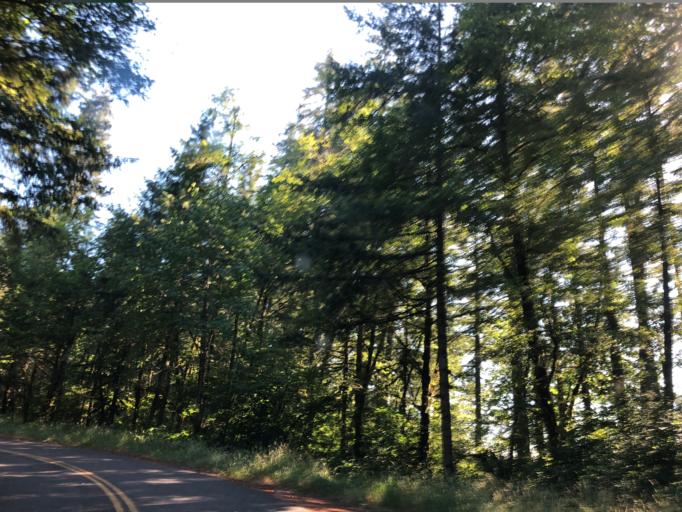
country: US
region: Oregon
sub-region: Linn County
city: Sweet Home
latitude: 44.4658
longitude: -122.6754
